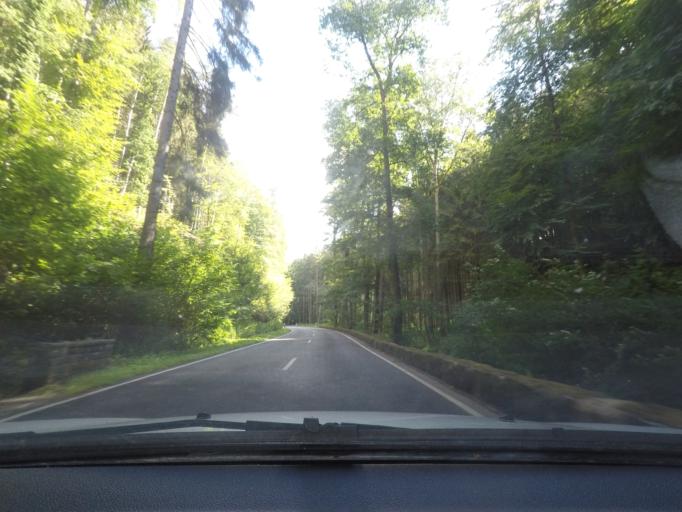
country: LU
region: Grevenmacher
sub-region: Canton d'Echternach
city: Waldbillig
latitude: 49.7627
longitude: 6.2788
